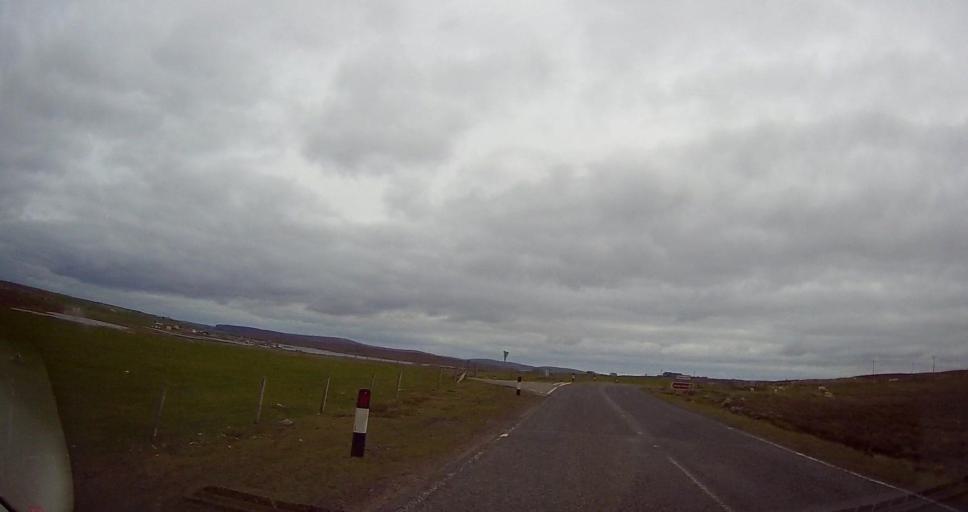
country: GB
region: Scotland
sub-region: Shetland Islands
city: Shetland
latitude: 60.7011
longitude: -0.9205
